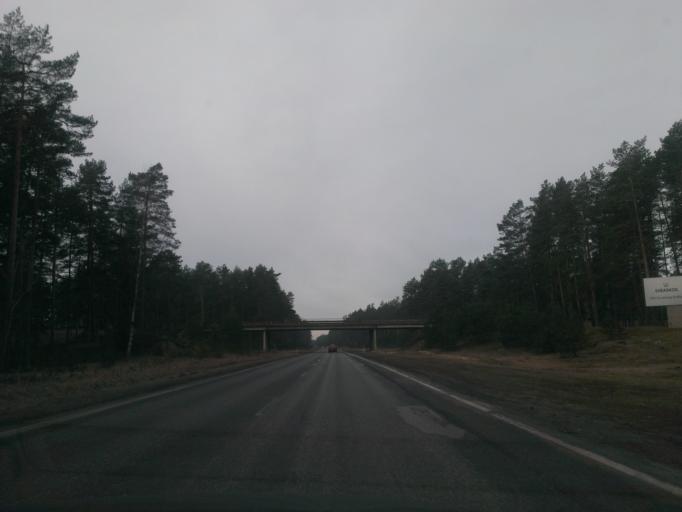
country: LV
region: Incukalns
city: Vangazi
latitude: 57.0811
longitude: 24.5232
